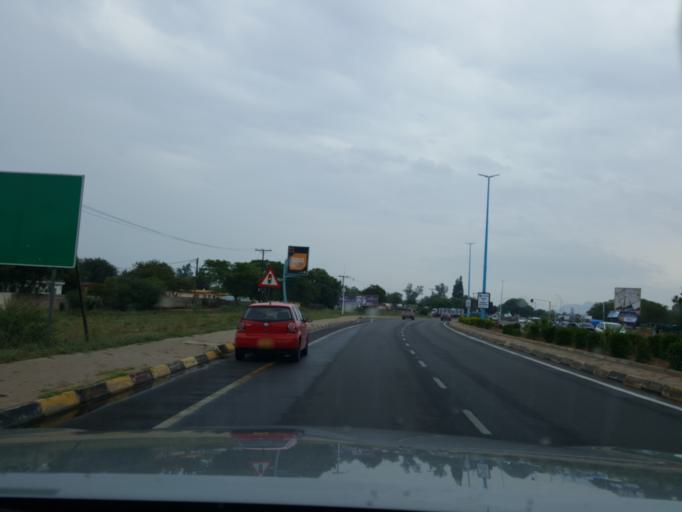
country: BW
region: South East
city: Gaborone
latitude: -24.6207
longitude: 25.9310
